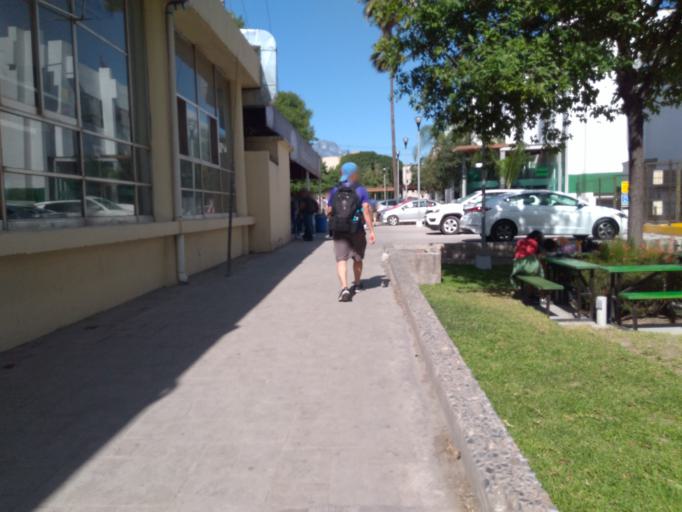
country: MX
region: Nuevo Leon
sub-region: San Nicolas de los Garza
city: San Nicolas de los Garza
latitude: 25.7250
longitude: -100.3141
